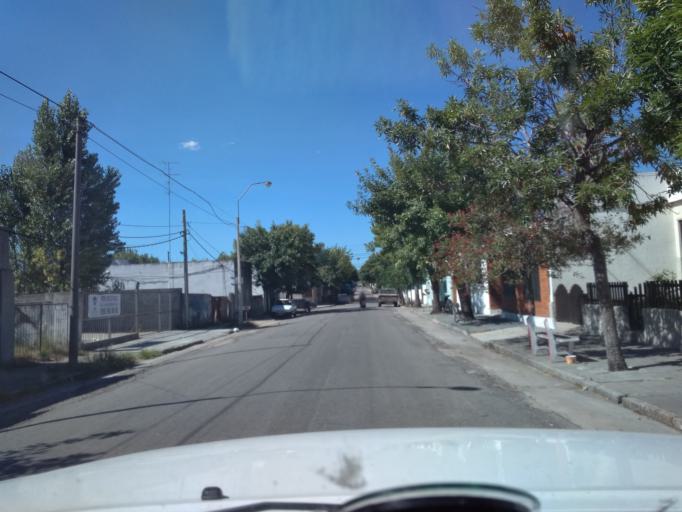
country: UY
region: Florida
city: Florida
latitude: -34.1015
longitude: -56.2191
